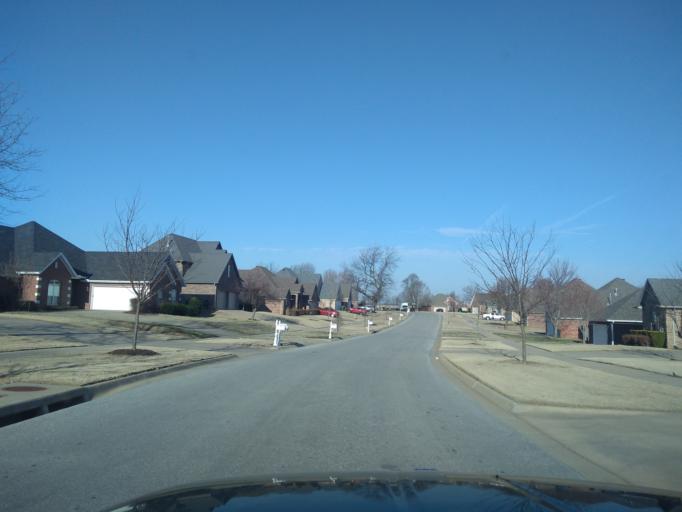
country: US
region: Arkansas
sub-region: Washington County
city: Farmington
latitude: 36.0711
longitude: -94.2504
